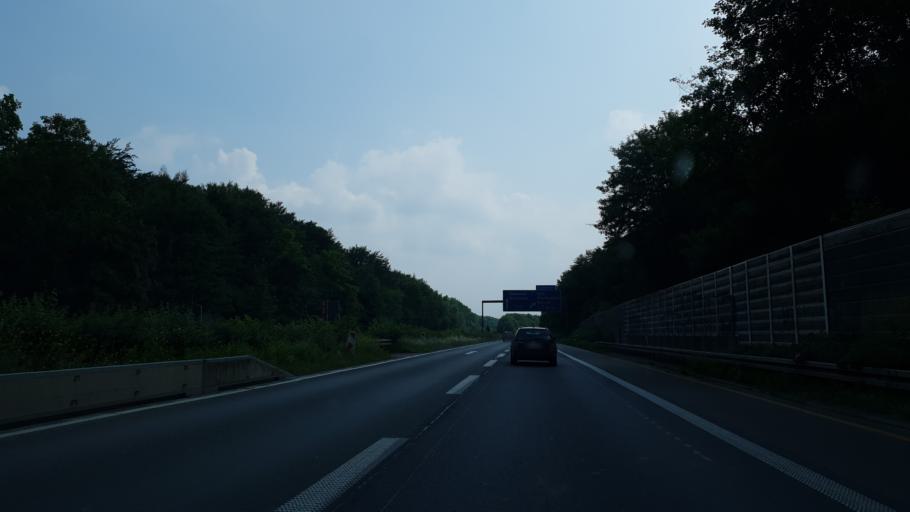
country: DE
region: North Rhine-Westphalia
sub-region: Regierungsbezirk Munster
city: Bottrop
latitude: 51.5628
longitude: 6.9281
